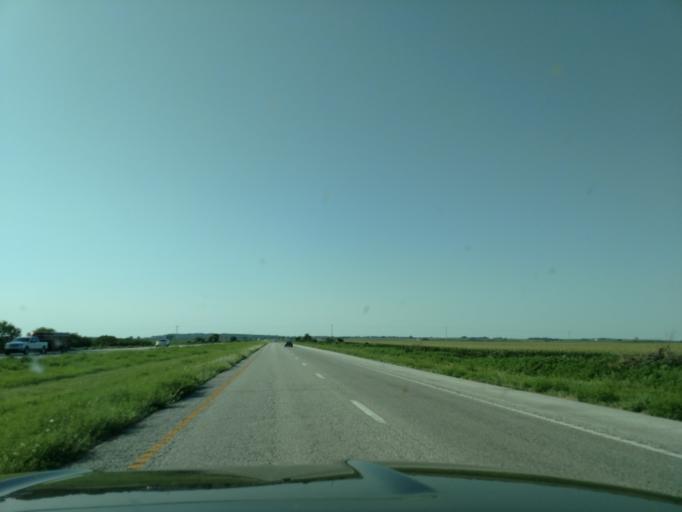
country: US
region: Missouri
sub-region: Atchison County
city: Rock Port
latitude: 40.4947
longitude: -95.5978
